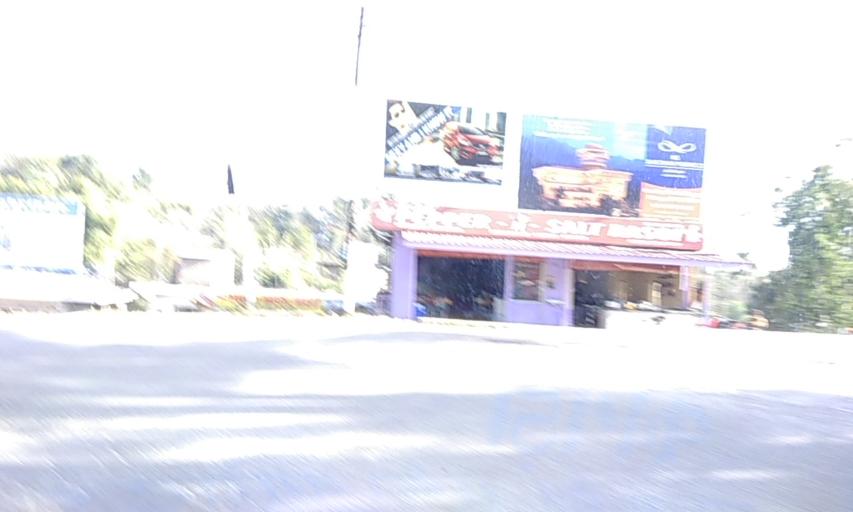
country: IN
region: Himachal Pradesh
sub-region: Kangra
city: Palampur
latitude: 32.0847
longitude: 76.5203
